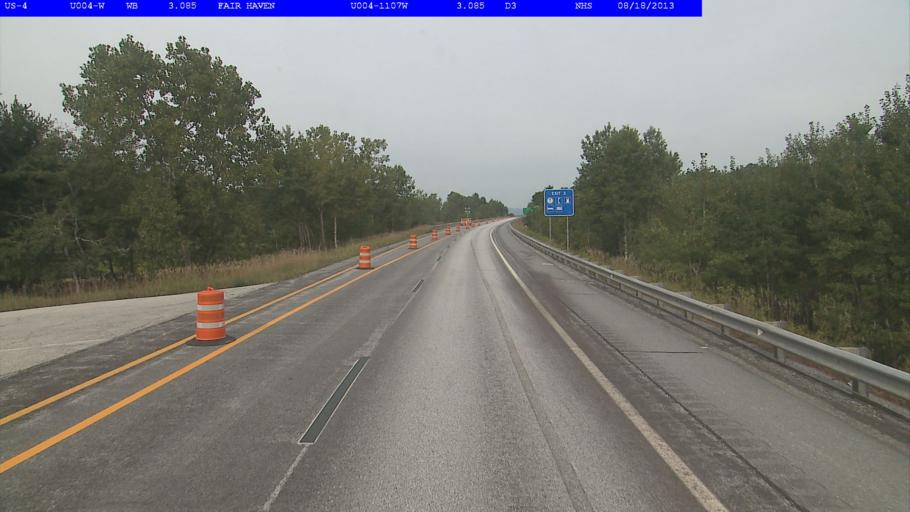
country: US
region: Vermont
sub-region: Rutland County
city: Fair Haven
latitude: 43.6054
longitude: -73.2497
